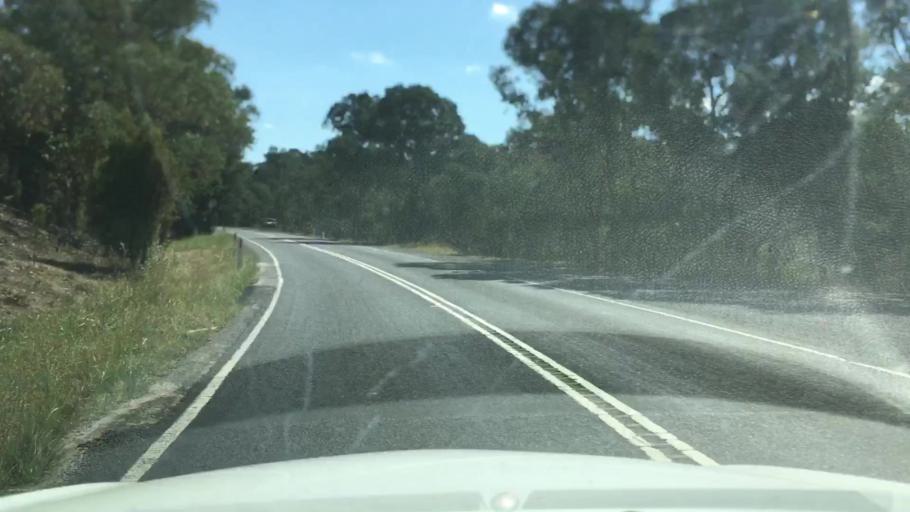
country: AU
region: Victoria
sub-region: Nillumbik
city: Saint Andrews
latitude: -37.6543
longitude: 145.2779
